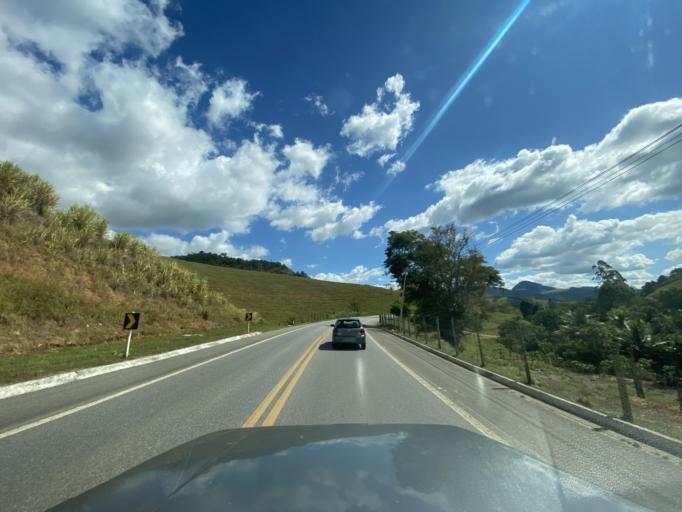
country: BR
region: Espirito Santo
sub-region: Jeronimo Monteiro
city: Jeronimo Monteiro
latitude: -20.7750
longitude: -41.4233
